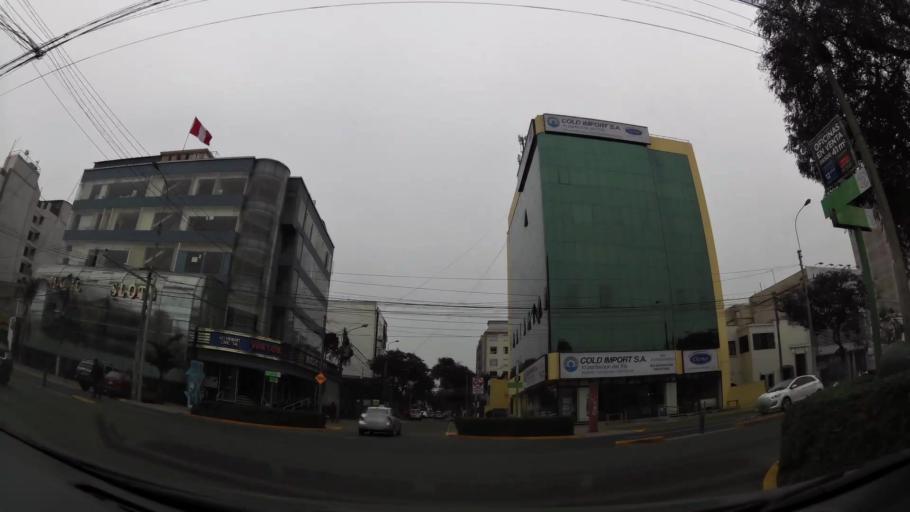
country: PE
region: Lima
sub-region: Lima
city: San Isidro
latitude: -12.1140
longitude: -77.0357
